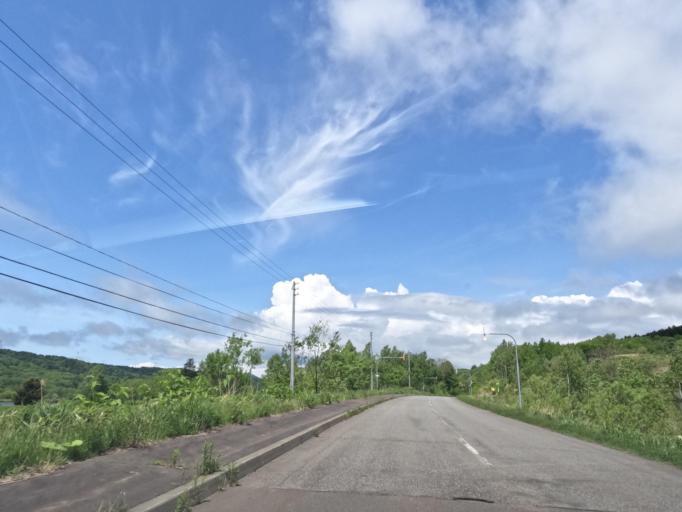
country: JP
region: Hokkaido
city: Tobetsu
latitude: 43.3697
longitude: 141.5739
